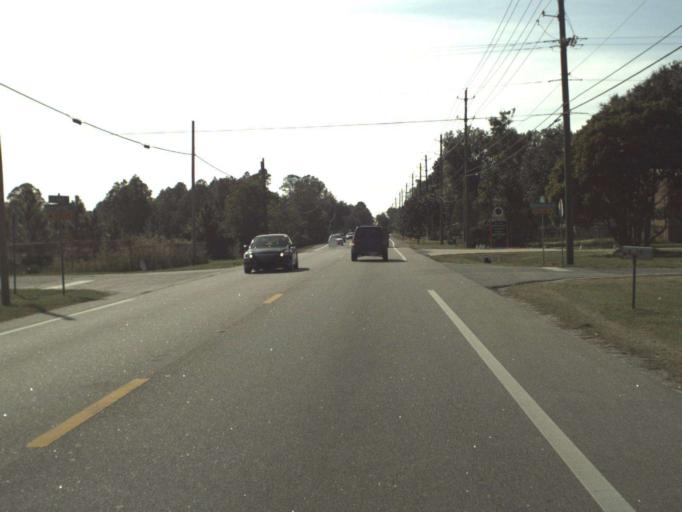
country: US
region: Florida
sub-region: Escambia County
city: Myrtle Grove
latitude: 30.3732
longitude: -87.3255
